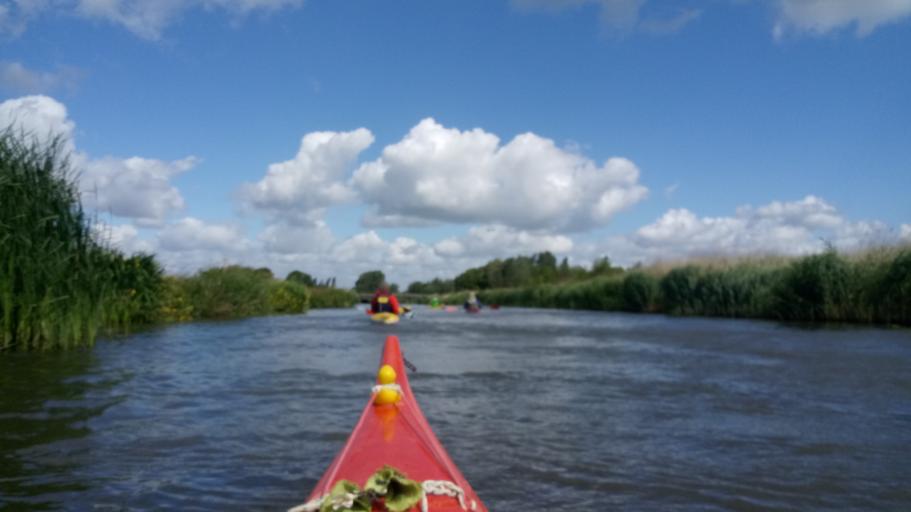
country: NL
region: North Holland
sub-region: Gemeente Enkhuizen
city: Enkhuizen
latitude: 52.7010
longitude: 5.2006
